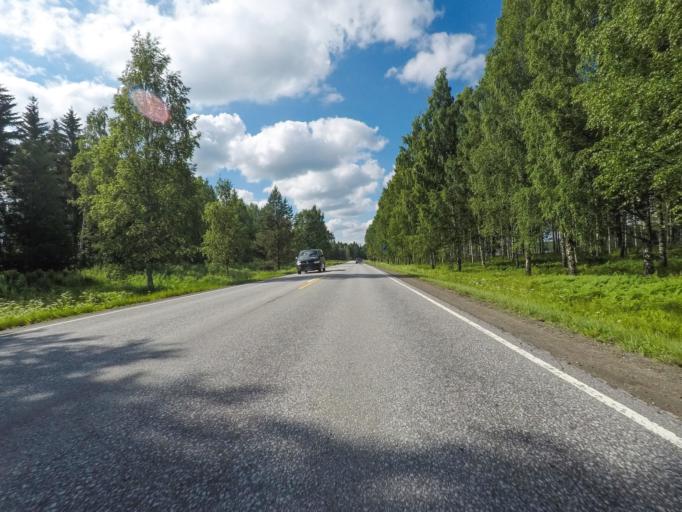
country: FI
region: Southern Savonia
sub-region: Savonlinna
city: Kerimaeki
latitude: 61.8091
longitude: 29.2726
